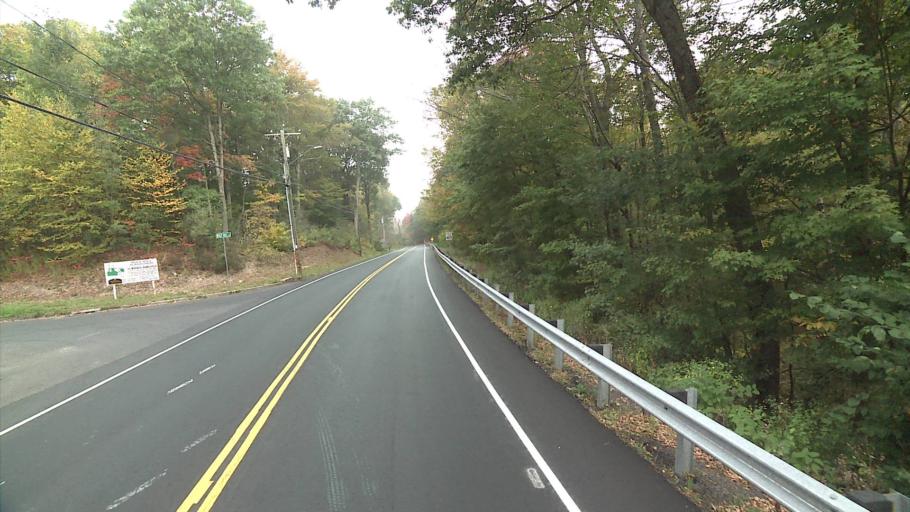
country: US
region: Connecticut
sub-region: Litchfield County
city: Watertown
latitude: 41.5986
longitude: -73.1527
